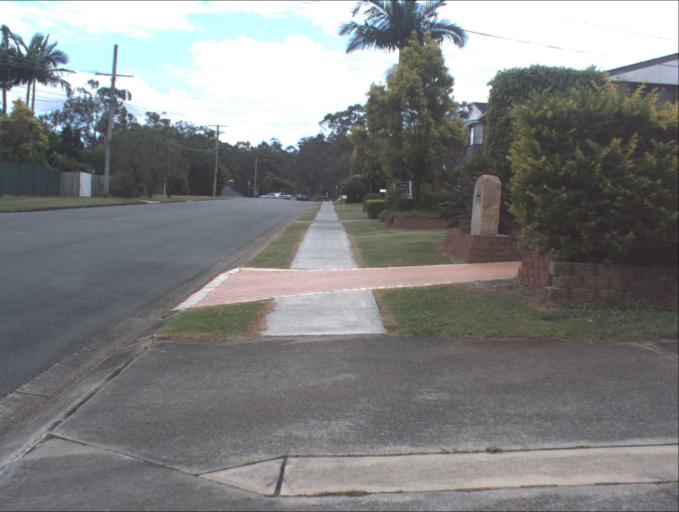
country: AU
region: Queensland
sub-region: Logan
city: Springwood
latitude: -27.6307
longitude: 153.1393
